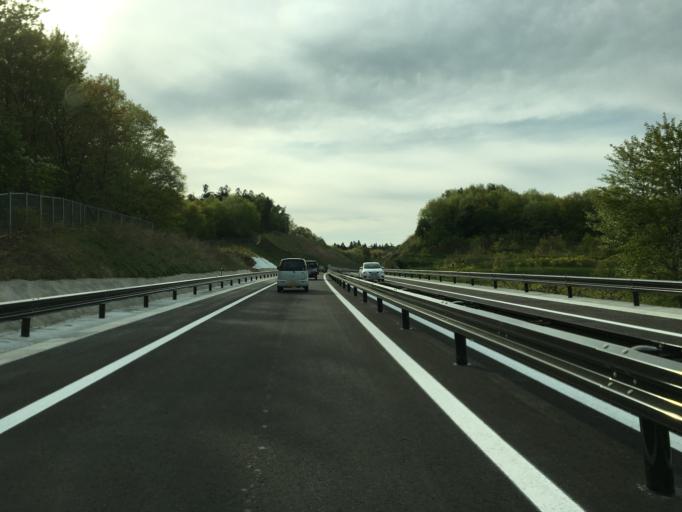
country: JP
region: Fukushima
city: Hobaramachi
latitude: 37.7900
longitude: 140.5562
